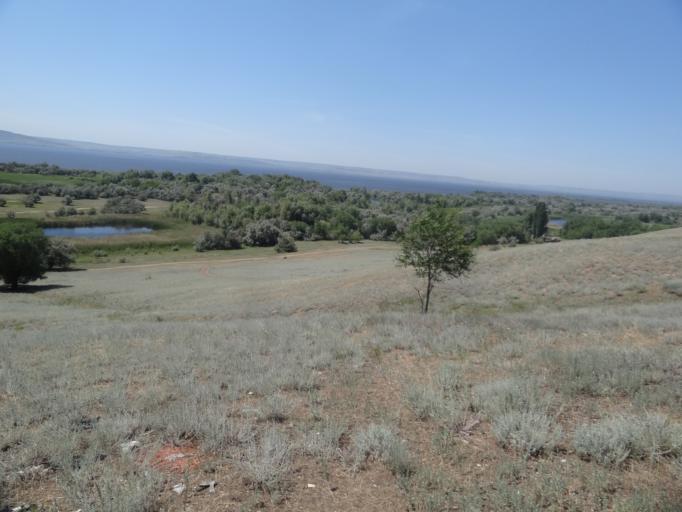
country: RU
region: Saratov
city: Krasnoarmeysk
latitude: 51.1272
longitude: 45.9412
